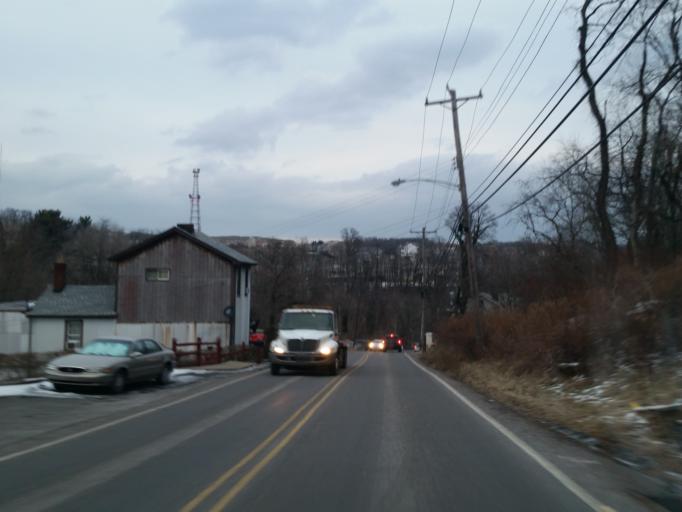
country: US
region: Pennsylvania
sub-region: Allegheny County
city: Brentwood
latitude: 40.3896
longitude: -79.9633
